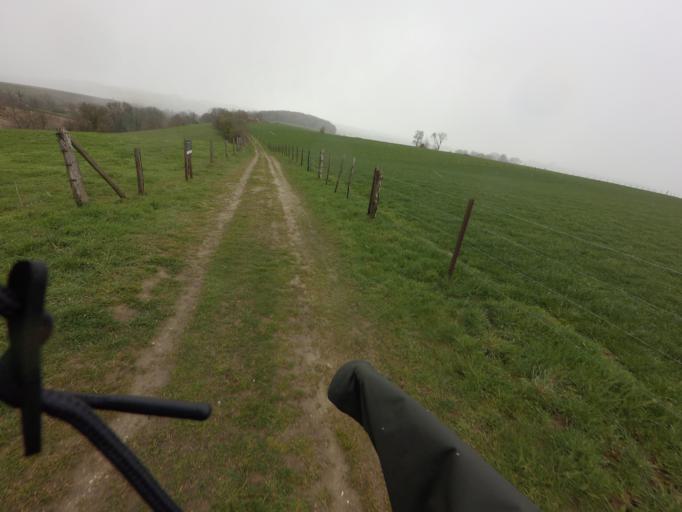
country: NL
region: Limburg
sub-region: Valkenburg aan de Geul
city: Schin op Geul
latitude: 50.8394
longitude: 5.8672
